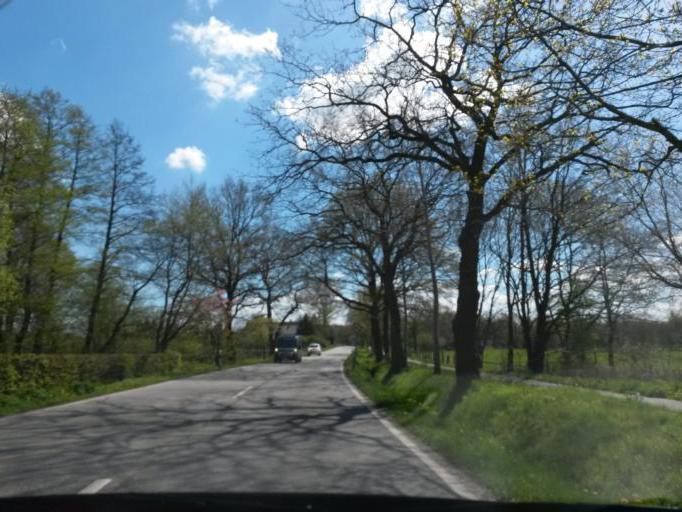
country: DE
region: Schleswig-Holstein
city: Holm
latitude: 53.6151
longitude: 9.6751
